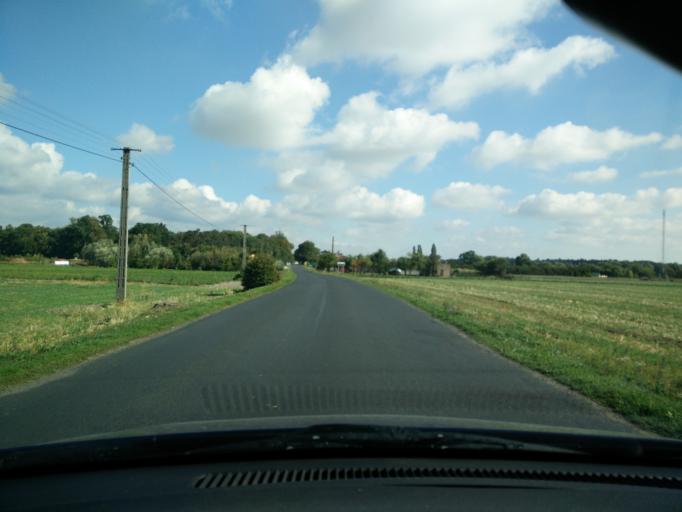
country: PL
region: Greater Poland Voivodeship
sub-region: Powiat sredzki
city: Dominowo
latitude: 52.3014
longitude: 17.3467
